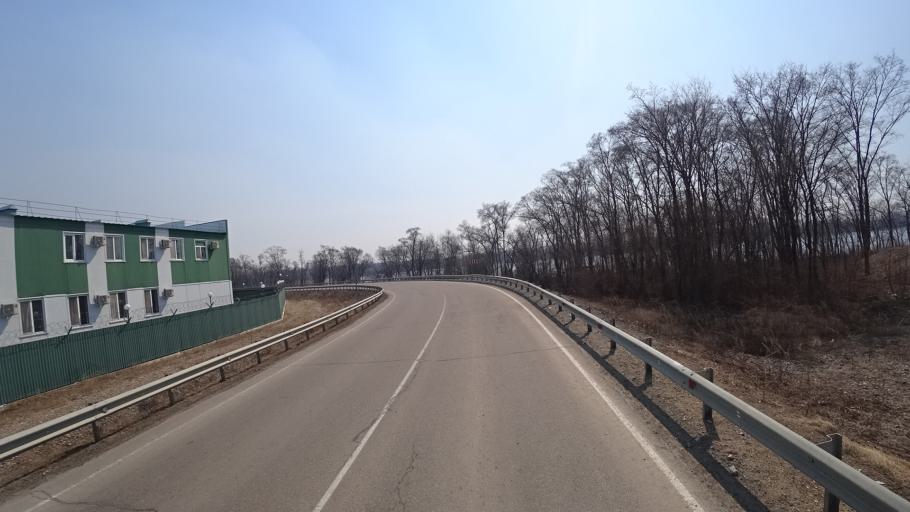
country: RU
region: Amur
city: Novobureyskiy
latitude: 49.7837
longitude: 129.9223
